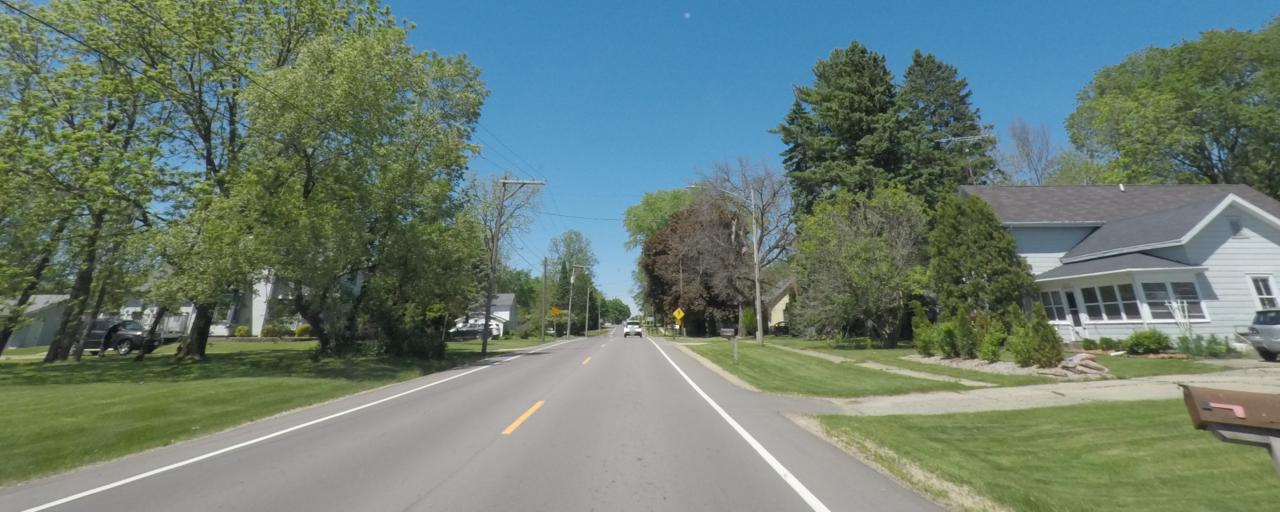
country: US
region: Wisconsin
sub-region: Green County
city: Brooklyn
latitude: 42.8481
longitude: -89.3692
